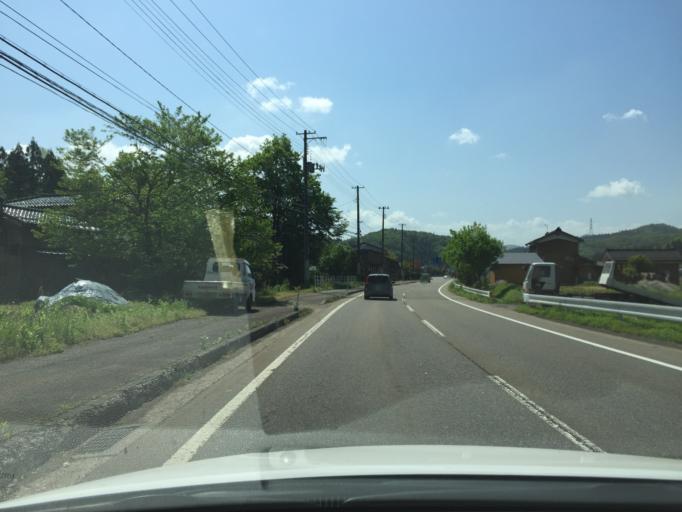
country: JP
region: Niigata
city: Kamo
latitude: 37.6114
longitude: 139.1039
